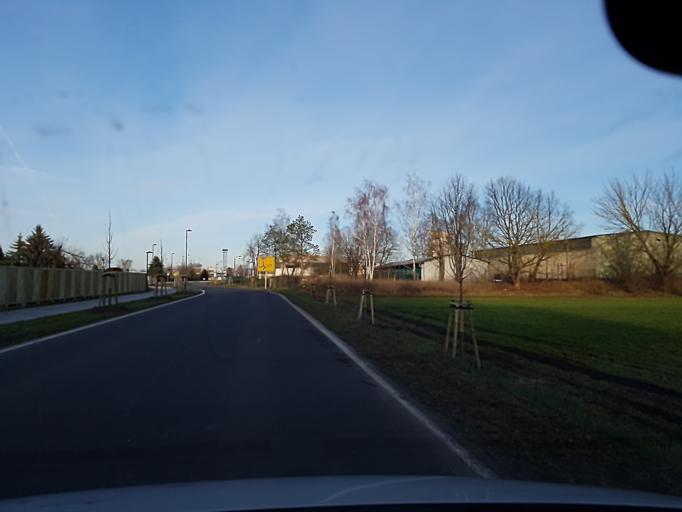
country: DE
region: Brandenburg
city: Finsterwalde
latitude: 51.6297
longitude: 13.7265
